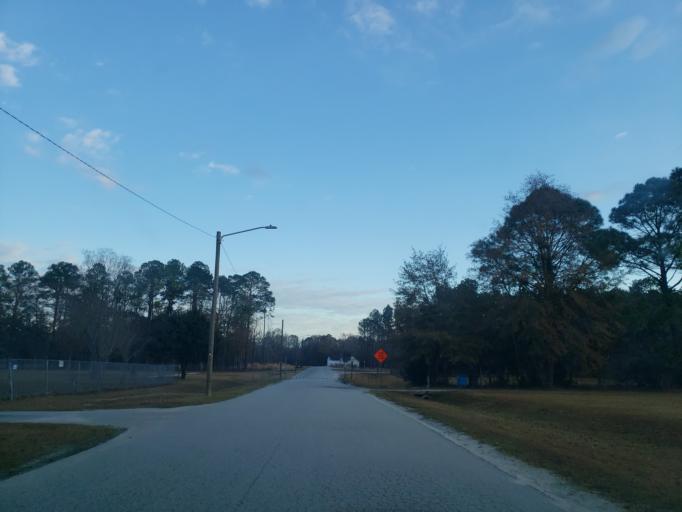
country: US
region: Georgia
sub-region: Chatham County
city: Bloomingdale
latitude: 32.1283
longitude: -81.3166
